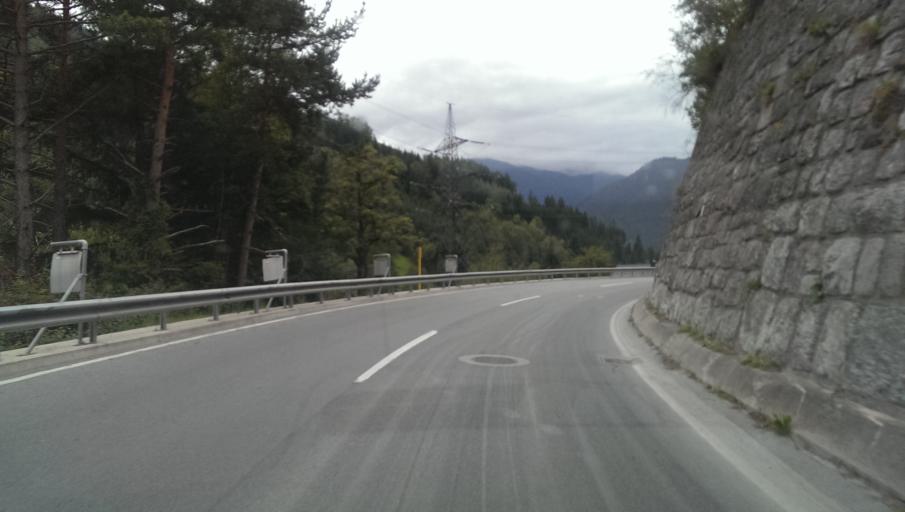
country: AT
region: Tyrol
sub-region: Politischer Bezirk Landeck
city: Grins
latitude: 47.1369
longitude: 10.5296
